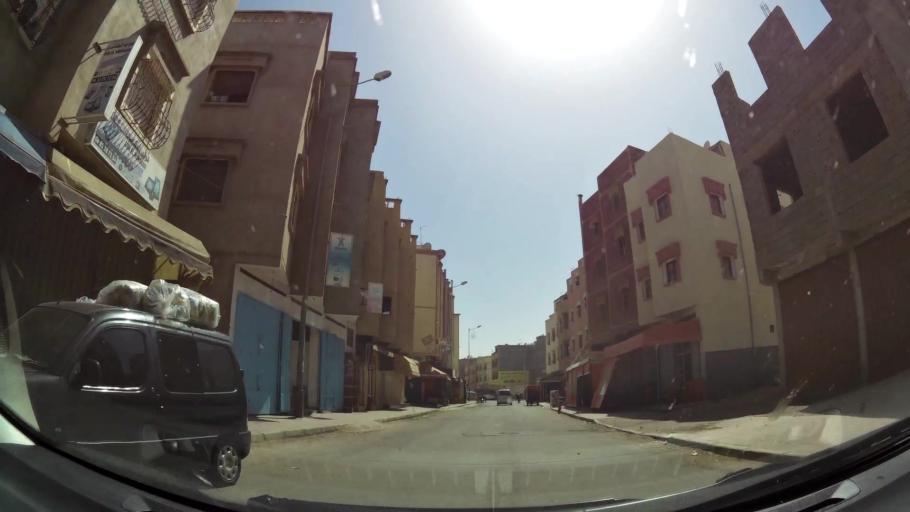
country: MA
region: Souss-Massa-Draa
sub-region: Inezgane-Ait Mellou
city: Inezgane
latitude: 30.3482
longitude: -9.5416
